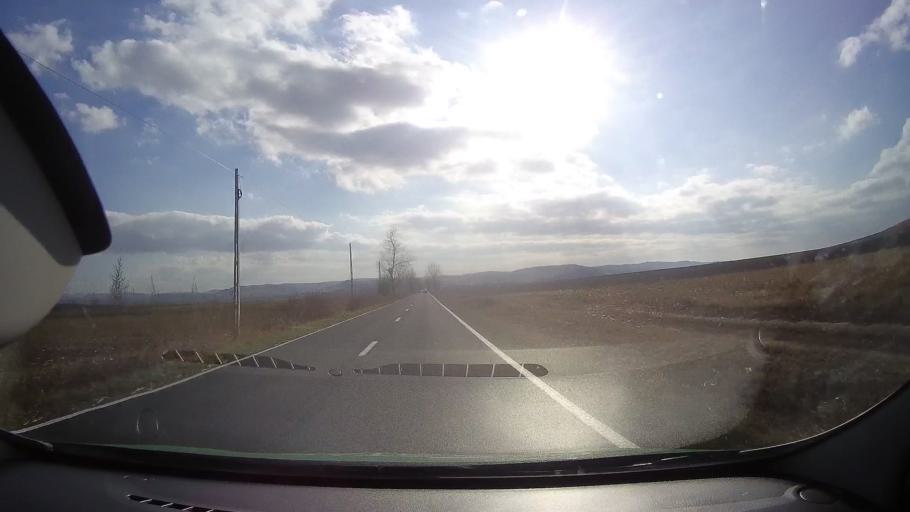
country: RO
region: Tulcea
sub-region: Comuna Nalbant
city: Nicolae Balcescu
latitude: 45.0117
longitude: 28.5991
